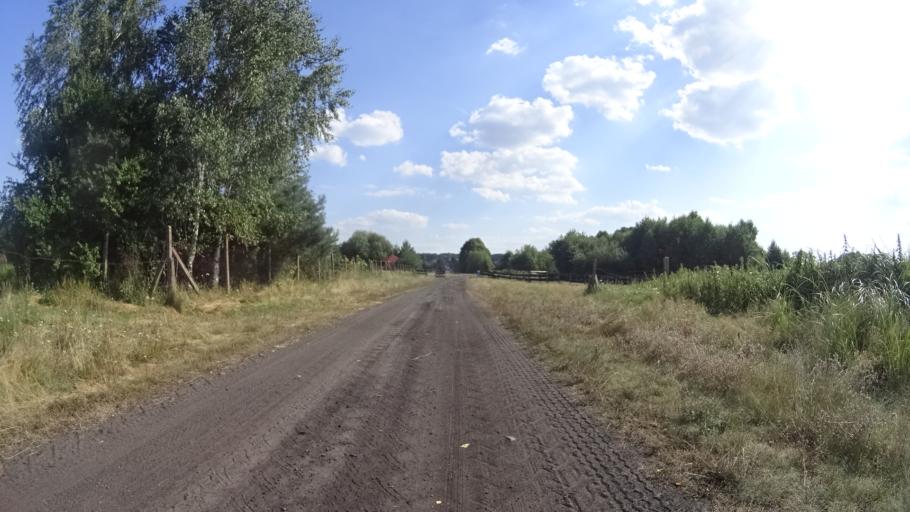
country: PL
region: Masovian Voivodeship
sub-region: Powiat bialobrzeski
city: Wysmierzyce
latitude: 51.6300
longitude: 20.8166
